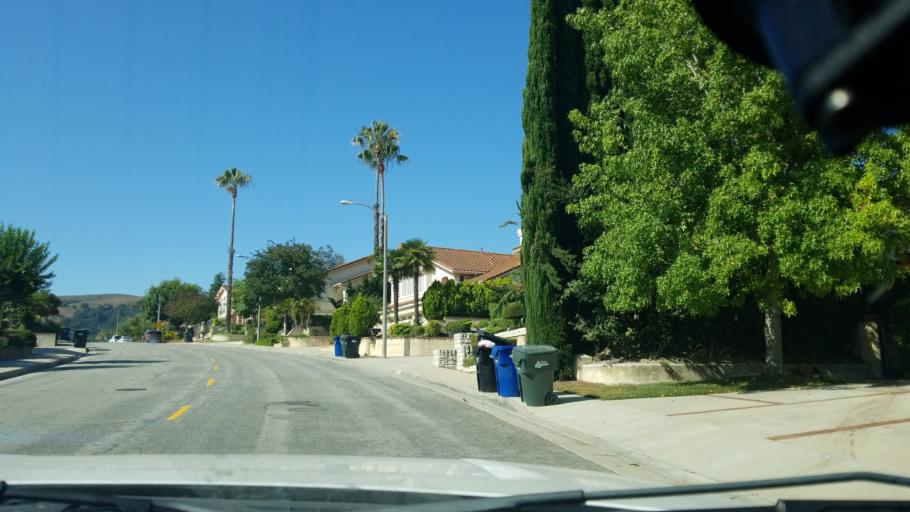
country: US
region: California
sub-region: Los Angeles County
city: Rowland Heights
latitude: 33.9850
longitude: -117.9251
